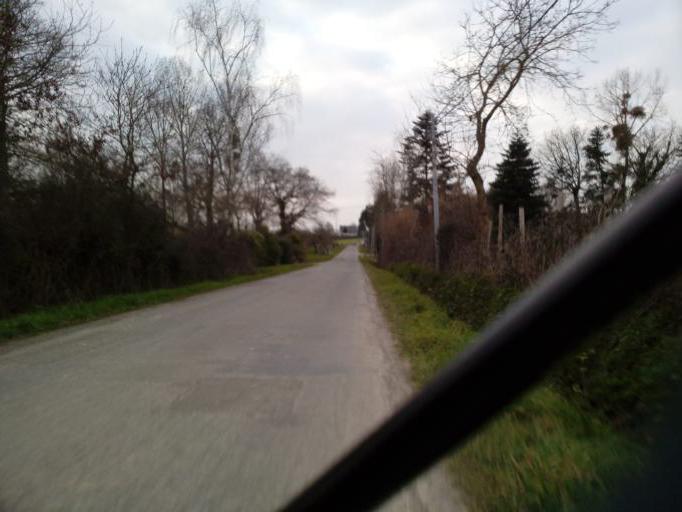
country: FR
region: Brittany
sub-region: Departement d'Ille-et-Vilaine
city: Cintre
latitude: 48.1062
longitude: -1.8940
